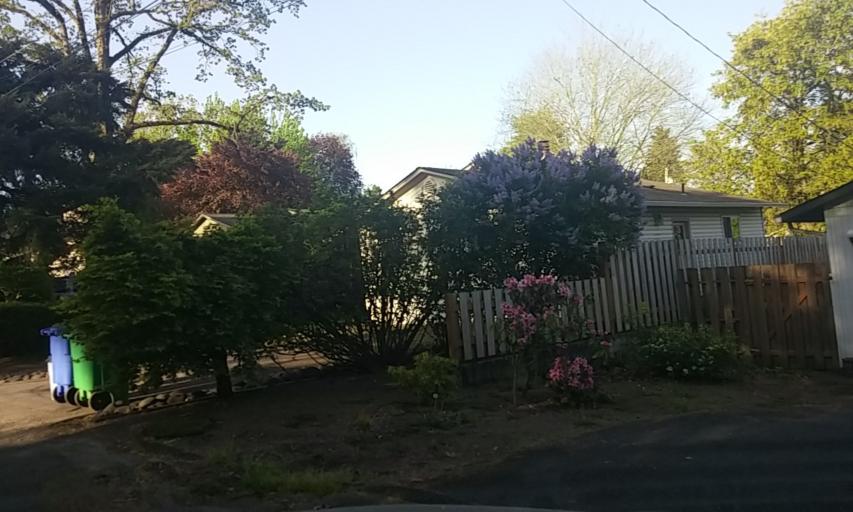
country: US
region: Oregon
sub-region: Washington County
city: Metzger
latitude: 45.4461
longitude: -122.7406
